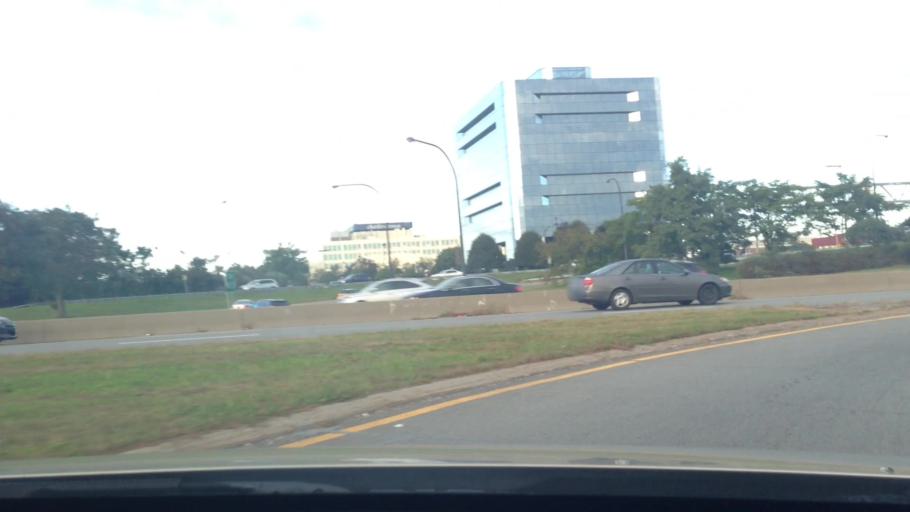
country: US
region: New York
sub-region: Nassau County
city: Carle Place
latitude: 40.7429
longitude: -73.6110
